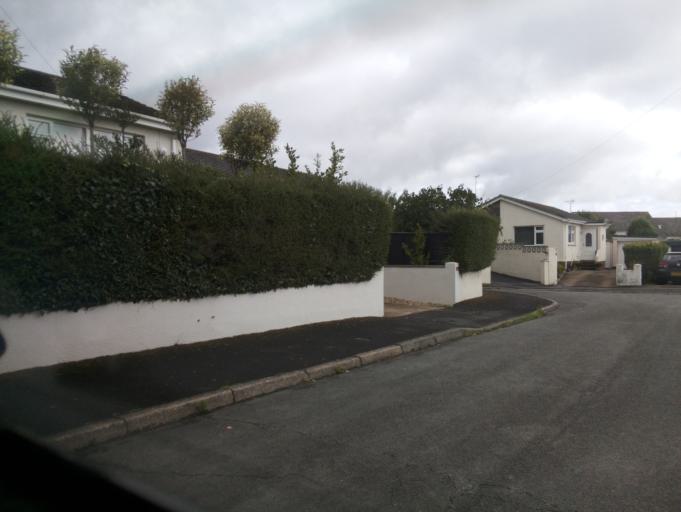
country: GB
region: England
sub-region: Devon
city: Dartmouth
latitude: 50.3292
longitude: -3.5990
